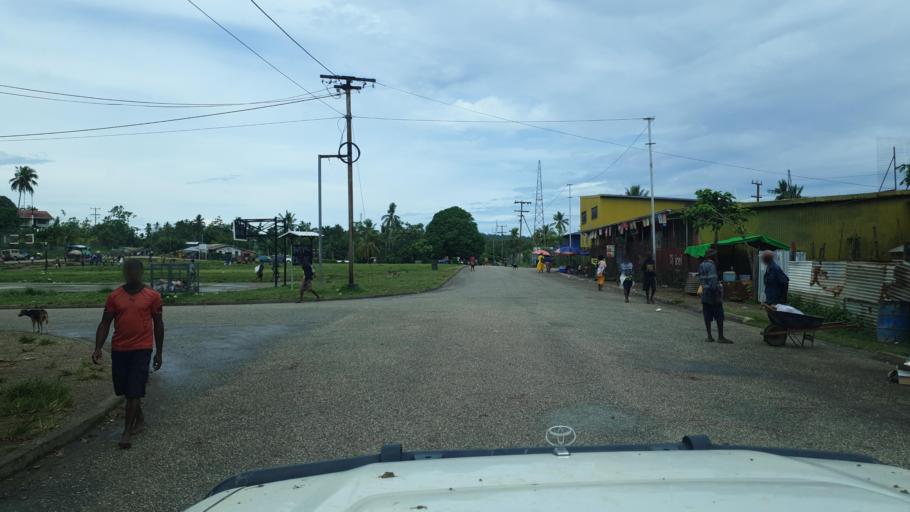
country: PG
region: Gulf
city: Kerema
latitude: -7.9597
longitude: 145.7719
